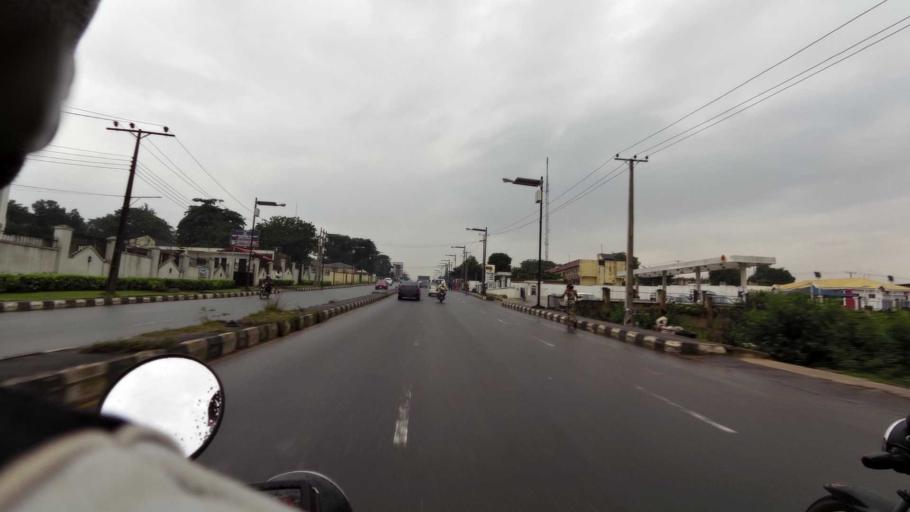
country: NG
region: Oyo
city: Ibadan
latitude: 7.3978
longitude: 3.9135
